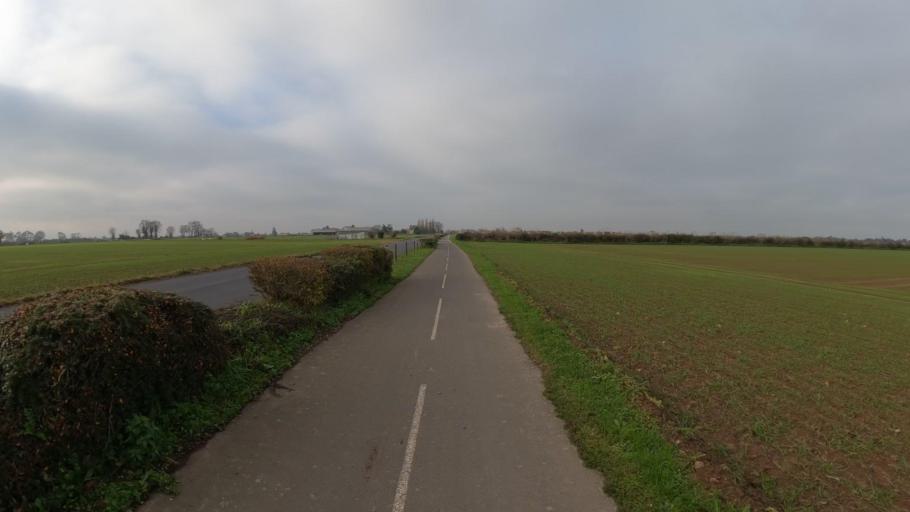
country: FR
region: Lower Normandy
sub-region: Departement du Calvados
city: Authie
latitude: 49.2025
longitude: -0.4192
